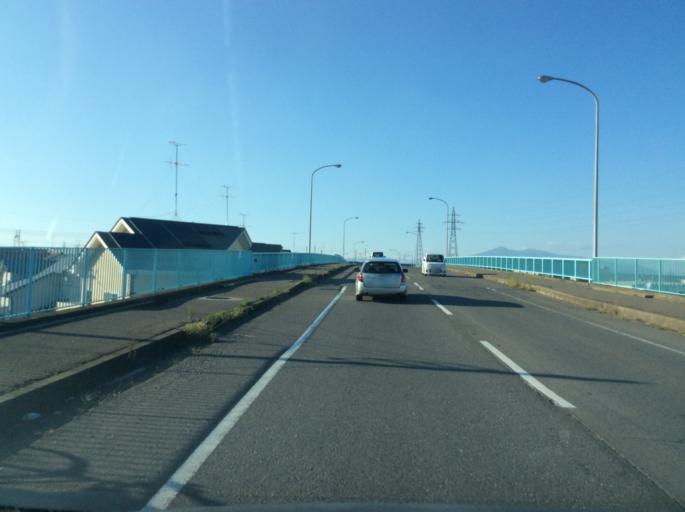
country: JP
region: Fukushima
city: Koriyama
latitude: 37.4103
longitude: 140.3966
